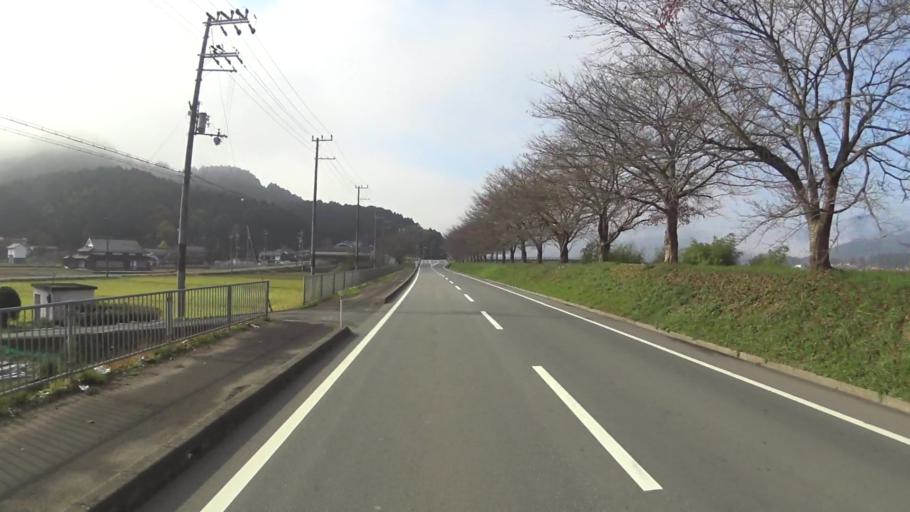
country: JP
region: Kyoto
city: Fukuchiyama
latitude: 35.2469
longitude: 135.1533
